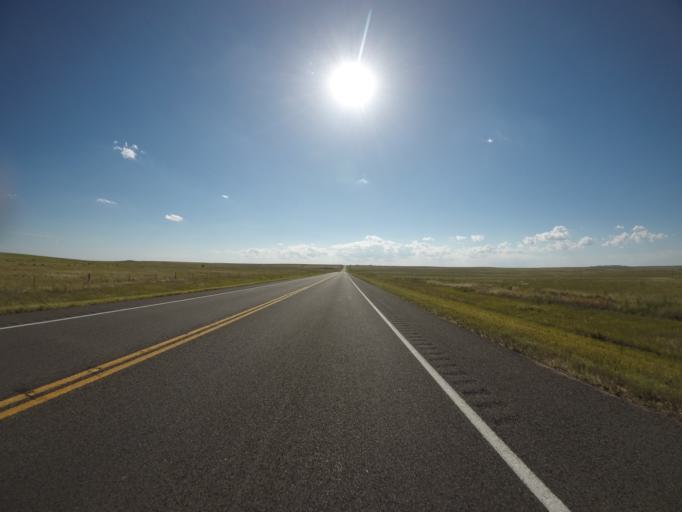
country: US
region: Colorado
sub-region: Morgan County
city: Brush
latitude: 40.6109
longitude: -103.5732
